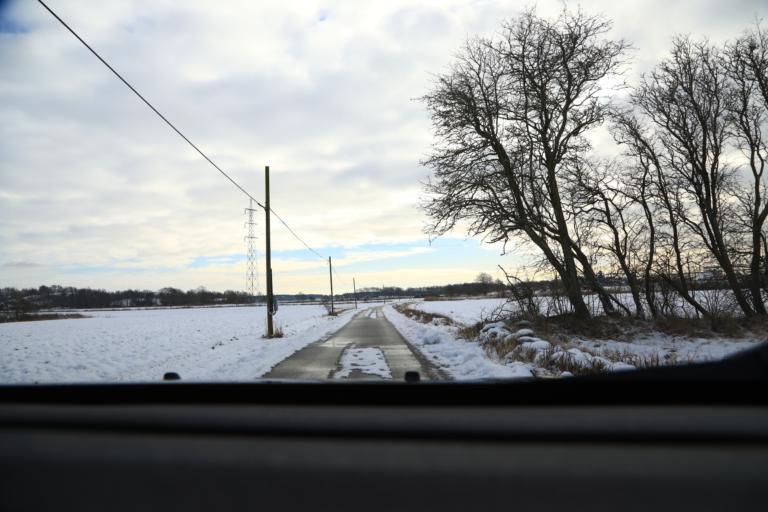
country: SE
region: Halland
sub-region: Kungsbacka Kommun
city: Frillesas
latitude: 57.2303
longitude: 12.1896
